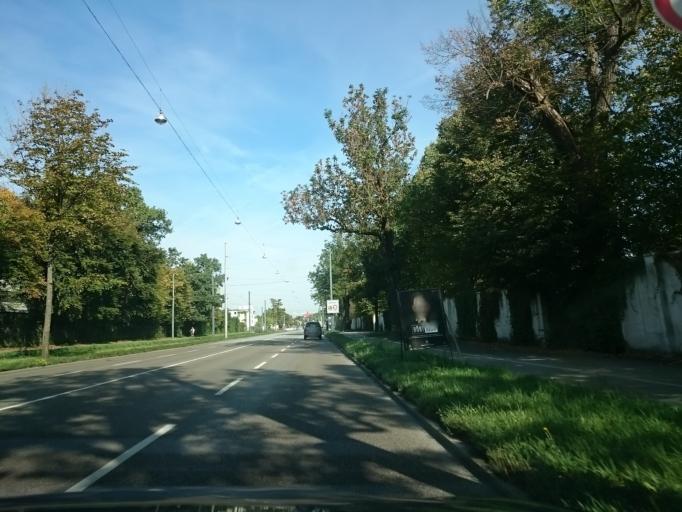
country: DE
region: Bavaria
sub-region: Swabia
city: Augsburg
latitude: 48.3443
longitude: 10.9057
